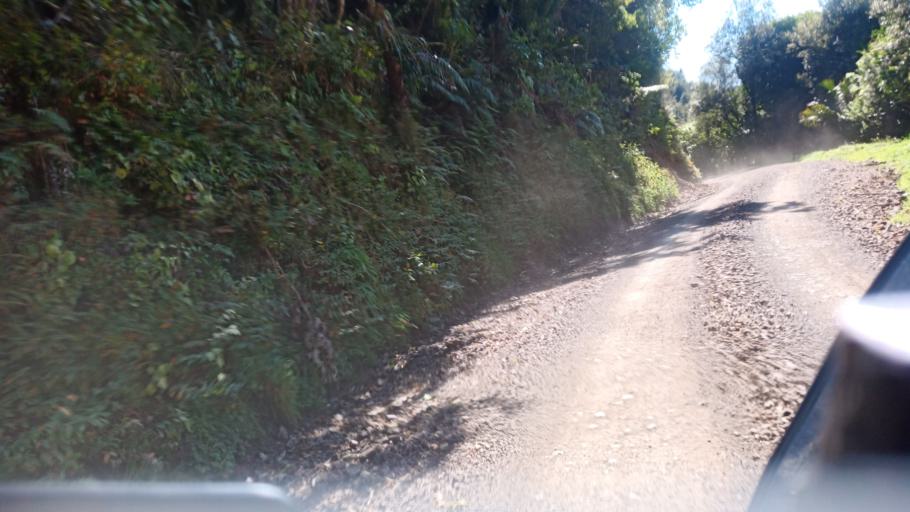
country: NZ
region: Bay of Plenty
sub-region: Opotiki District
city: Opotiki
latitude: -38.0783
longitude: 177.4751
